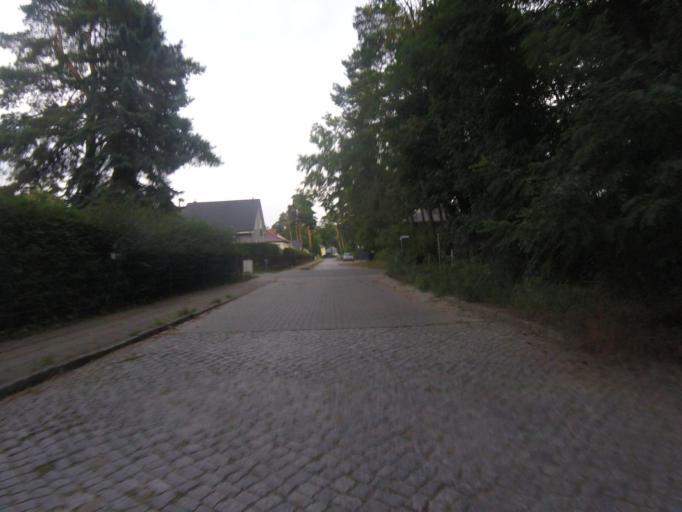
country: DE
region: Brandenburg
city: Zeuthen
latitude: 52.3503
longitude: 13.6136
